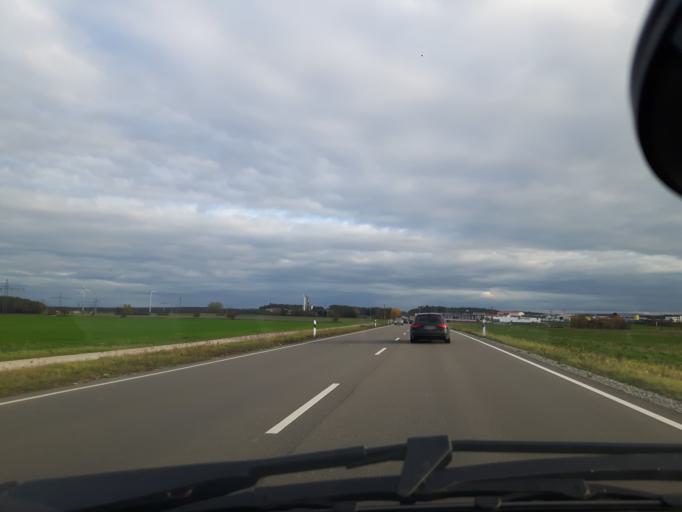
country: DE
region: Bavaria
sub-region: Regierungsbezirk Mittelfranken
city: Burgoberbach
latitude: 49.2489
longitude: 10.5955
